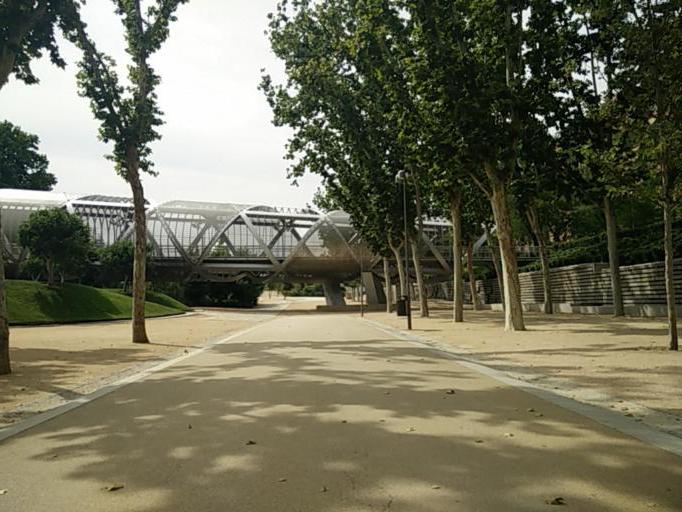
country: ES
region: Madrid
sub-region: Provincia de Madrid
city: Arganzuela
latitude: 40.3987
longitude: -3.7099
